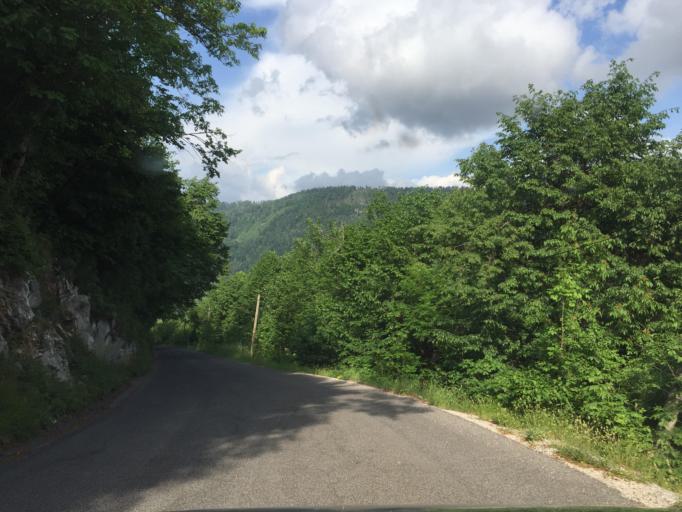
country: SI
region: Nova Gorica
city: Sempas
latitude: 46.0407
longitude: 13.7802
